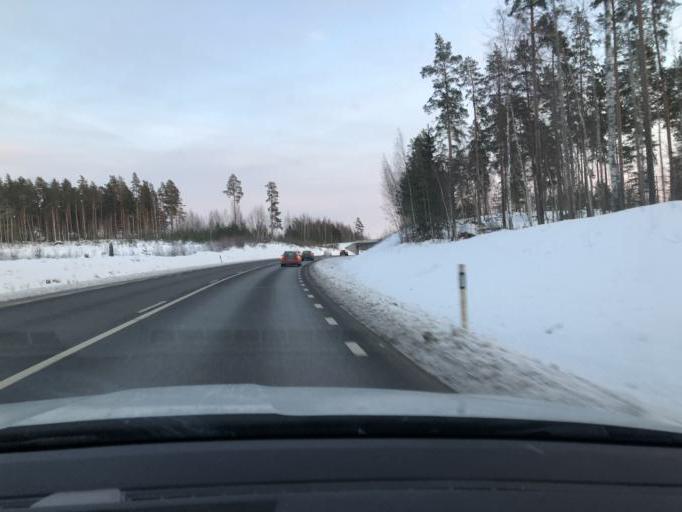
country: SE
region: Dalarna
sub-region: Faluns Kommun
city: Falun
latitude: 60.6047
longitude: 15.6716
